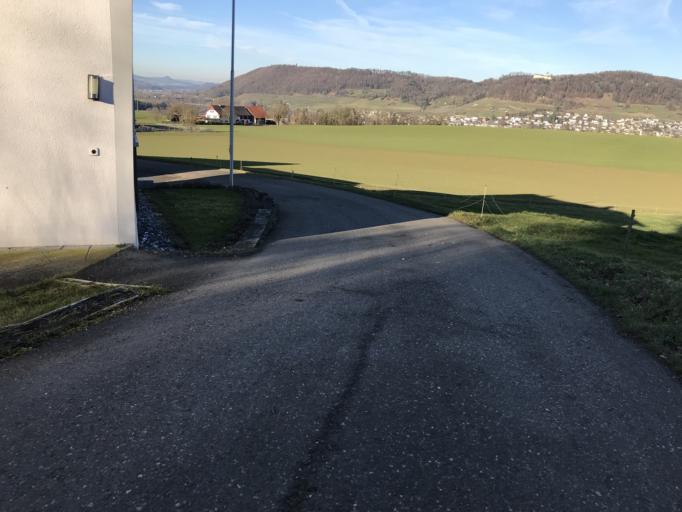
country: CH
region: Thurgau
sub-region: Frauenfeld District
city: Wagenhausen
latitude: 47.6453
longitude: 8.8494
